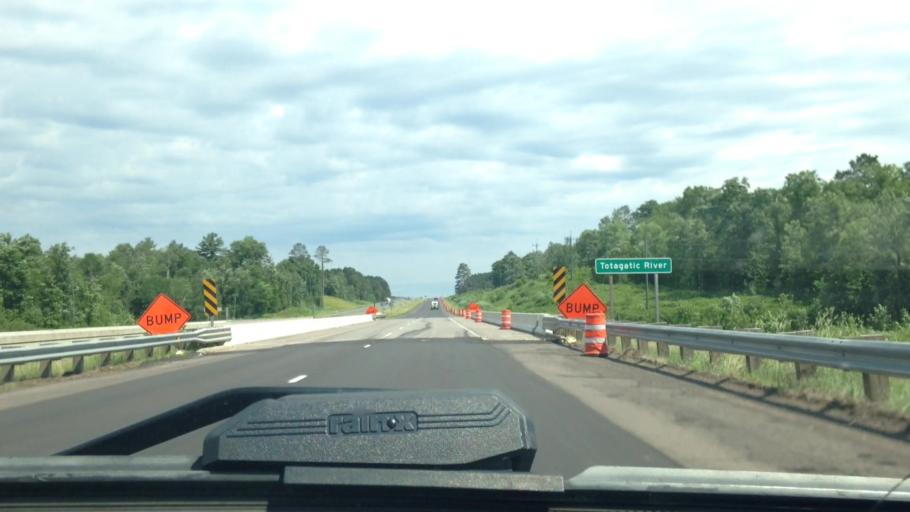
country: US
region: Wisconsin
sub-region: Washburn County
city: Spooner
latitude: 46.1426
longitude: -91.8147
